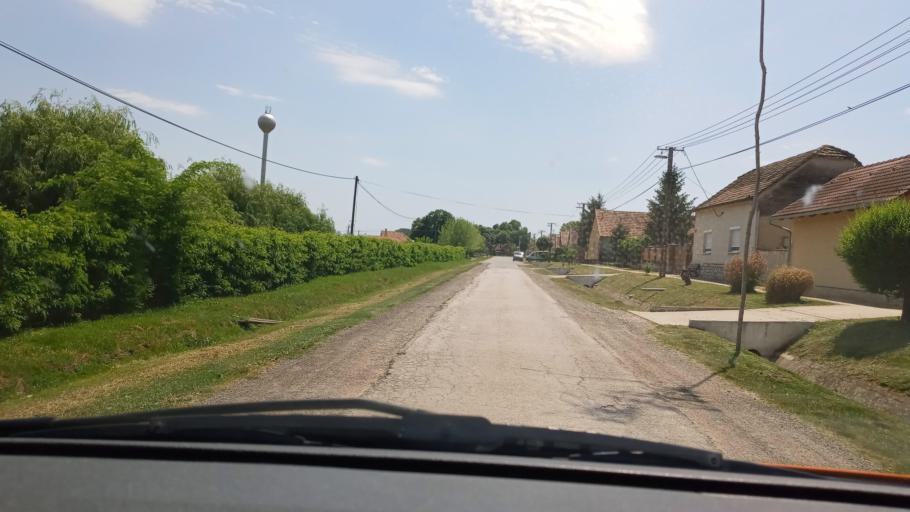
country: HU
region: Baranya
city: Harkany
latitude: 45.8311
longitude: 18.1374
